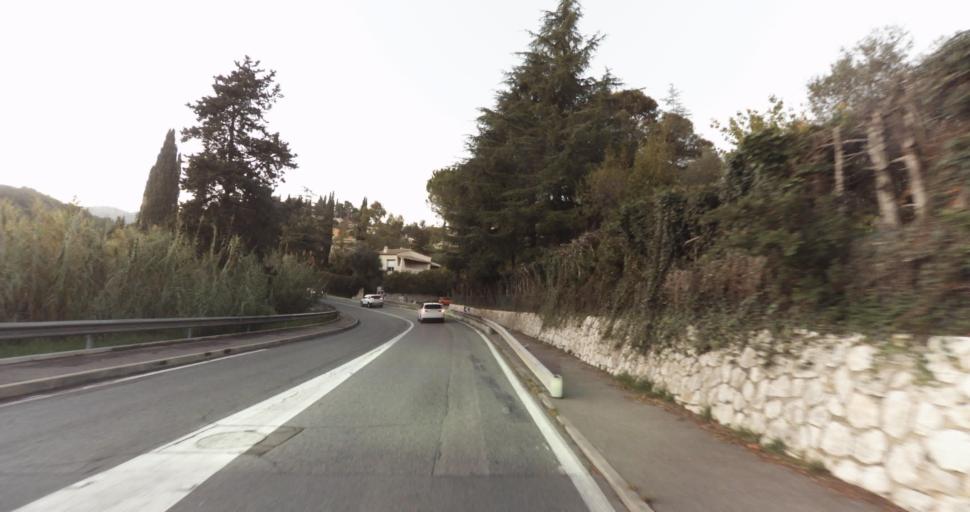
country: FR
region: Provence-Alpes-Cote d'Azur
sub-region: Departement des Alpes-Maritimes
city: Saint-Paul-de-Vence
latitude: 43.7119
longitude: 7.1249
